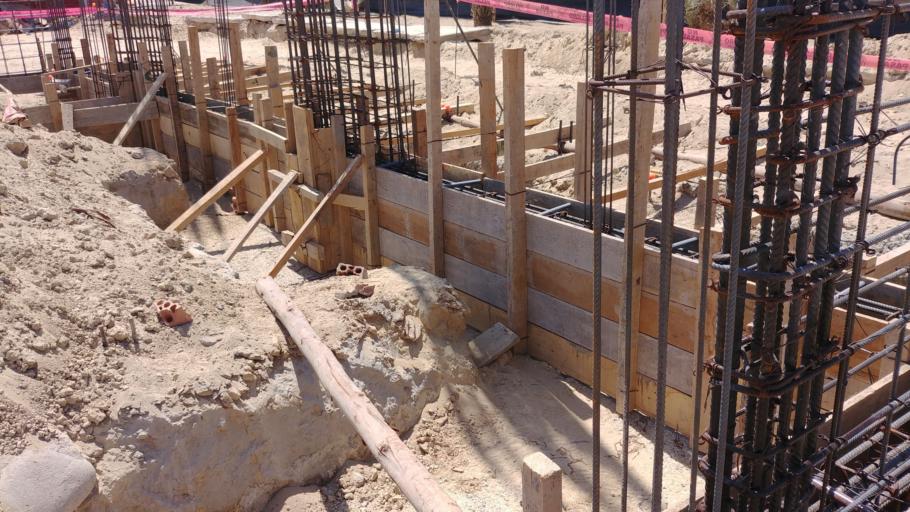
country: PE
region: Ica
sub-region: Provincia de Pisco
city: Villa Tupac Amaru
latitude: -13.8342
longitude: -76.1407
